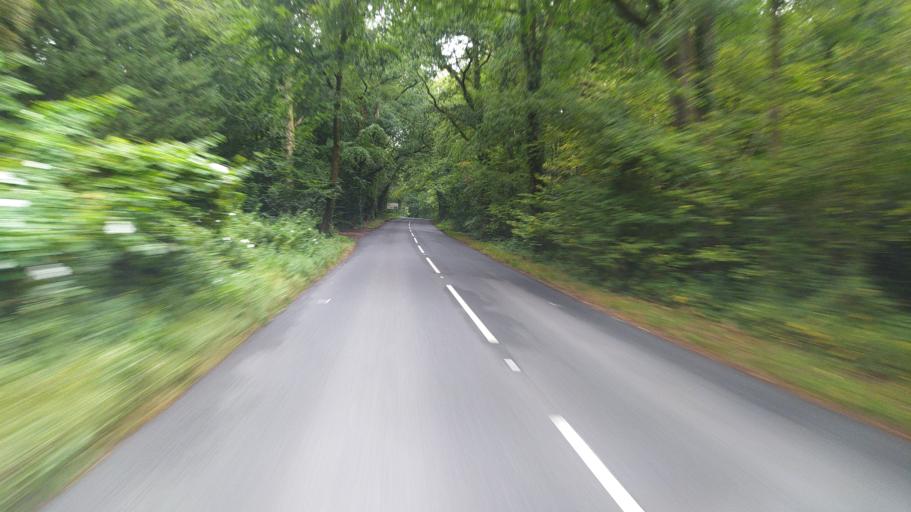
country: GB
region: England
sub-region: Dorset
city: Verwood
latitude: 50.8866
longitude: -1.9101
